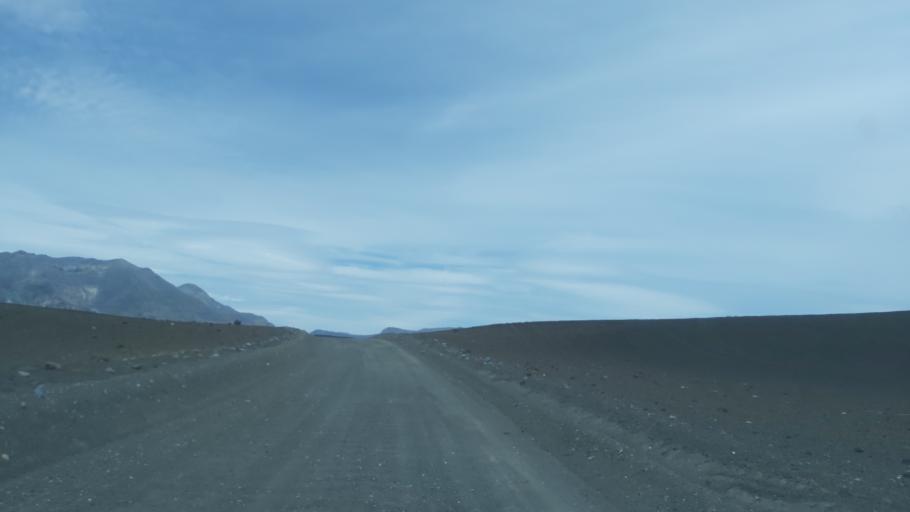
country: AR
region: Neuquen
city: Andacollo
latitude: -37.4341
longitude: -71.2854
